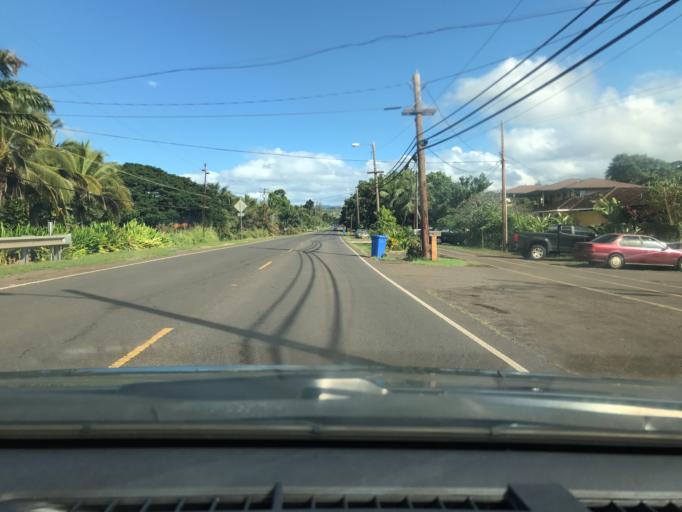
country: US
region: Hawaii
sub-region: Honolulu County
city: Hale'iwa
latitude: 21.5759
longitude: -158.1160
